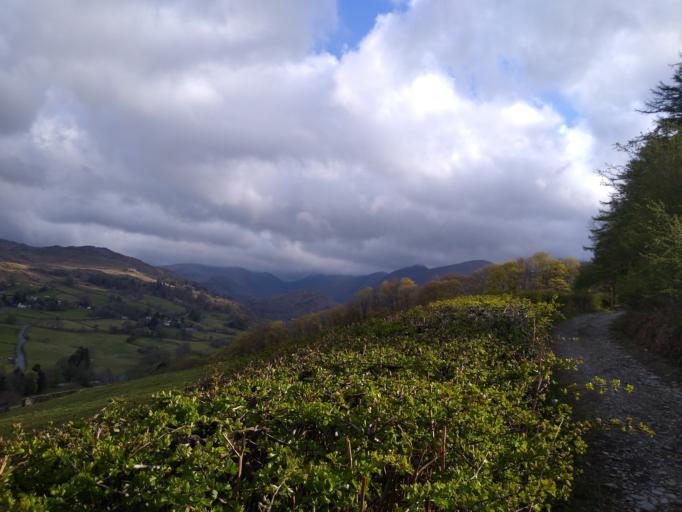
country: GB
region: England
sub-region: Cumbria
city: Windermere
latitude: 54.4153
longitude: -2.9019
